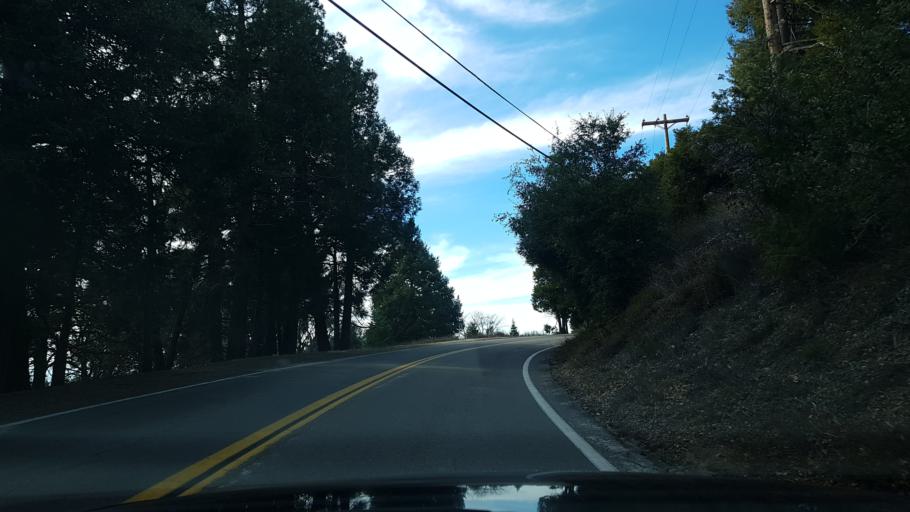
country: US
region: California
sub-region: Riverside County
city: Aguanga
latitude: 33.3165
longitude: -116.8767
